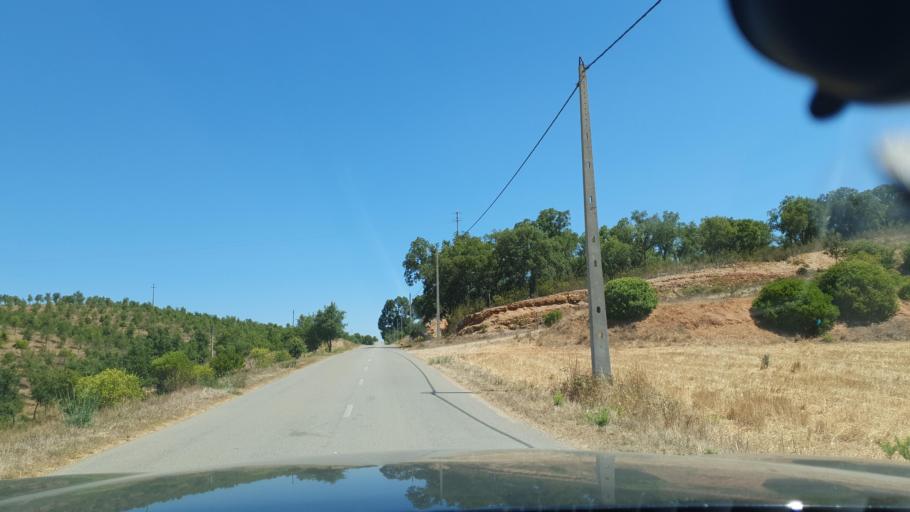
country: PT
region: Beja
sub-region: Odemira
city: Odemira
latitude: 37.5460
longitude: -8.4595
